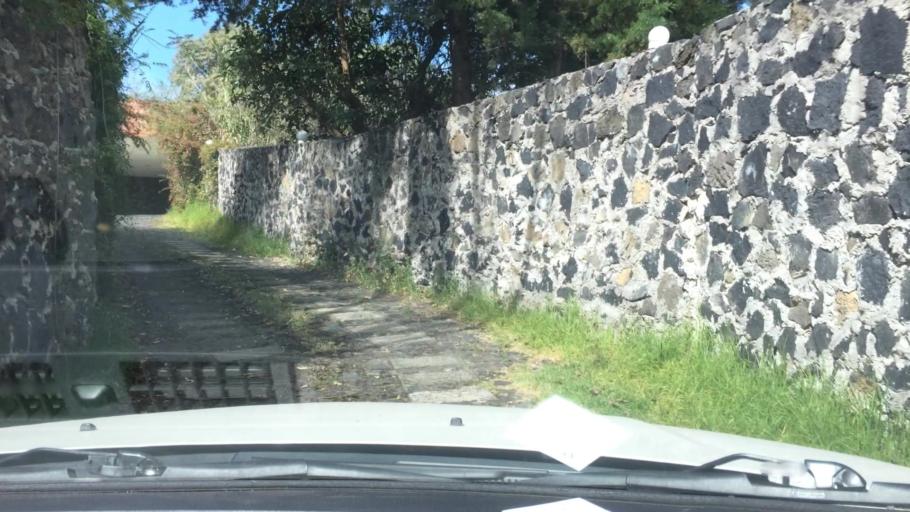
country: MX
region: Mexico City
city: Xochimilco
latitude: 19.2339
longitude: -99.1545
